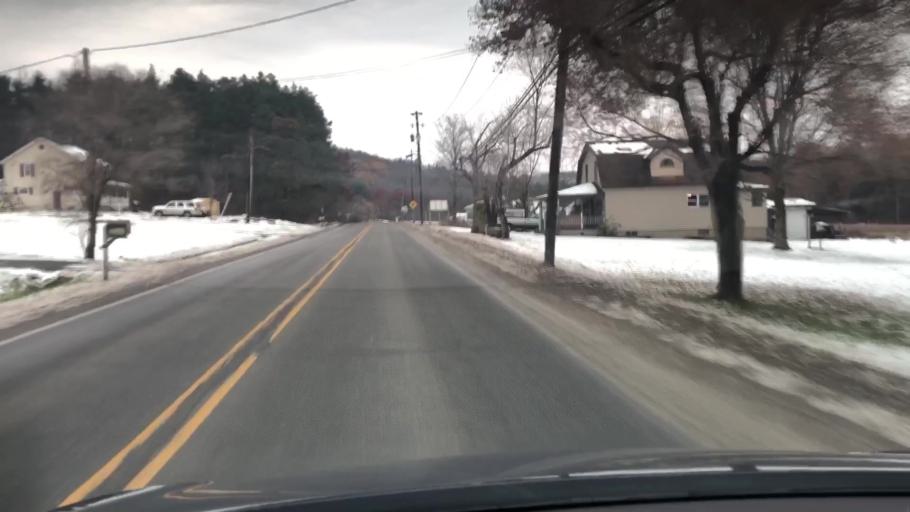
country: US
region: Pennsylvania
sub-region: Jefferson County
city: Brookville
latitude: 41.1225
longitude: -79.1844
